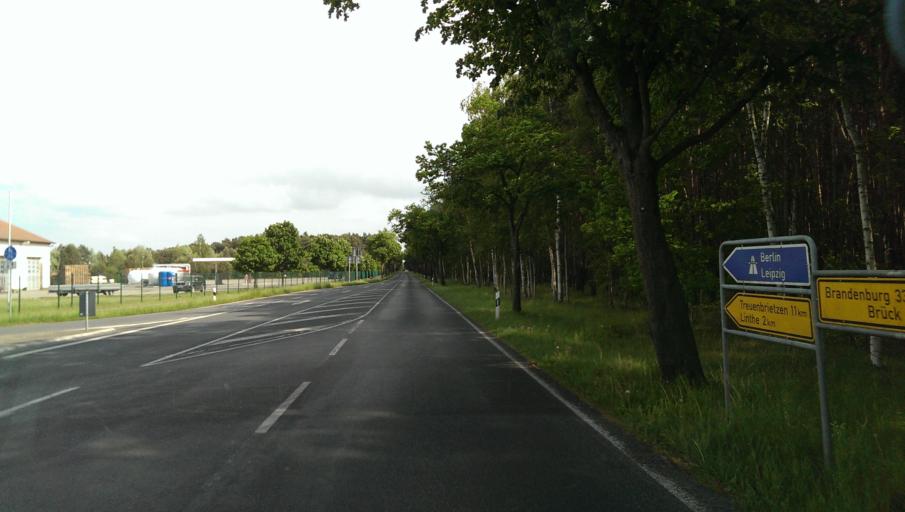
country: DE
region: Brandenburg
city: Linthe
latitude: 52.1692
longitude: 12.7674
